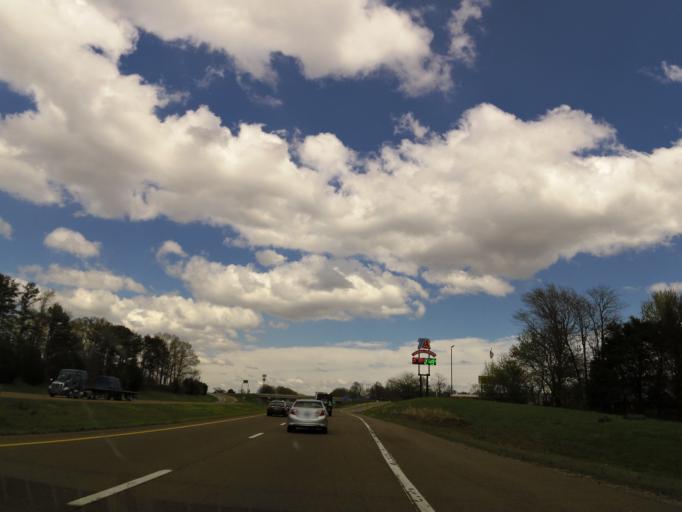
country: US
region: Tennessee
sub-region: Crockett County
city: Bells
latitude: 35.5954
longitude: -89.0584
